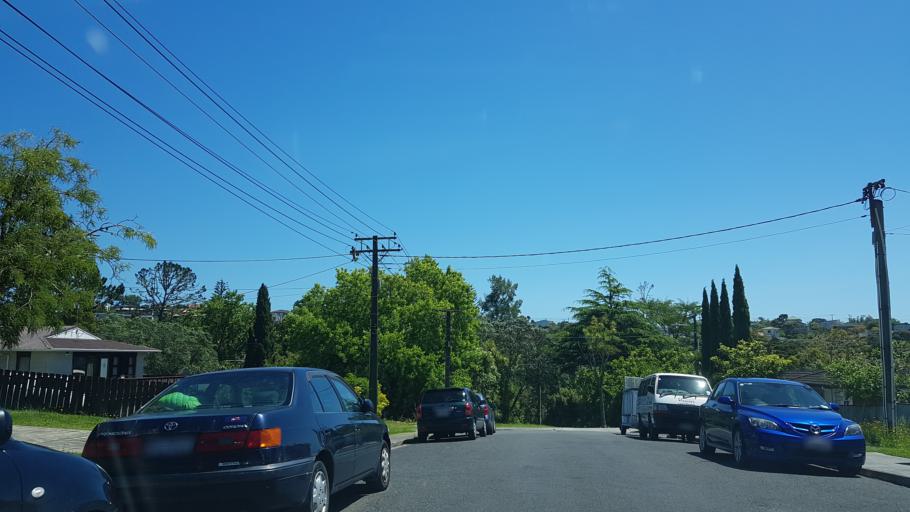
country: NZ
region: Auckland
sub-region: Auckland
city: North Shore
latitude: -36.8080
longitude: 174.7293
